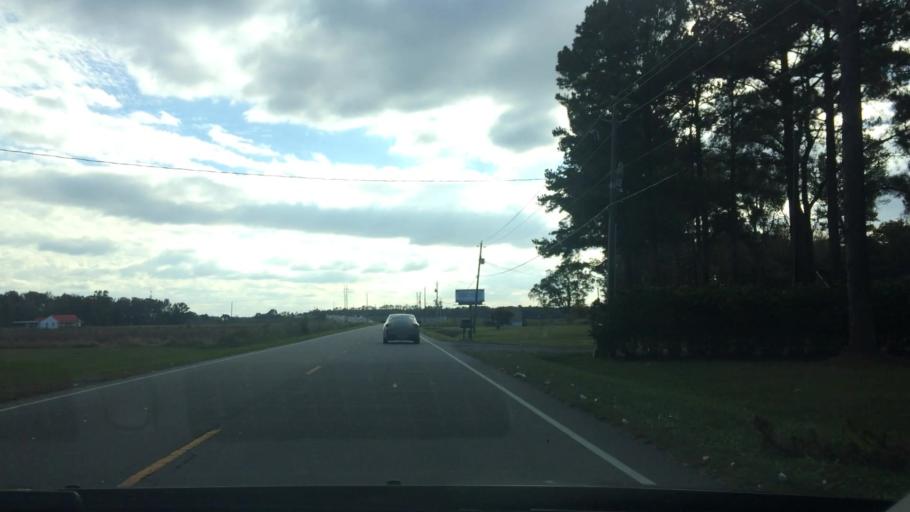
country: US
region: North Carolina
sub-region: Wayne County
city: Elroy
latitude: 35.4196
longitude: -77.8931
